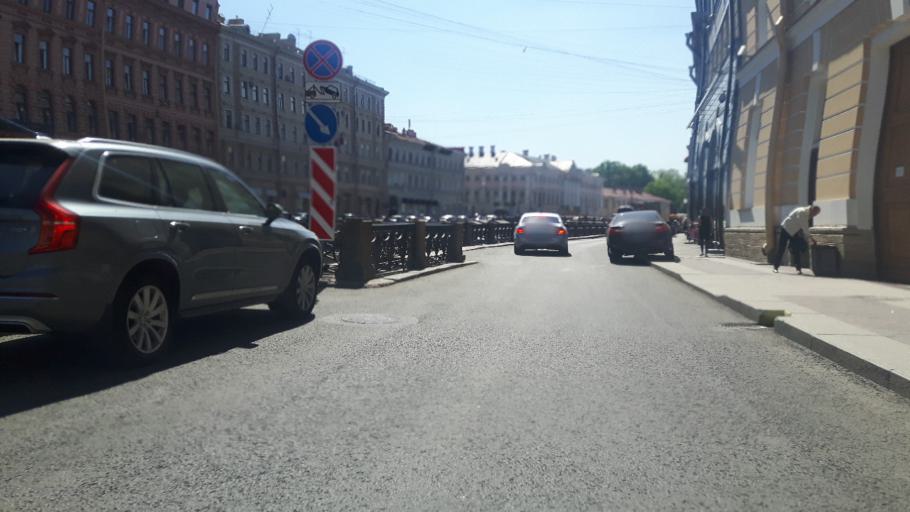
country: RU
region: St.-Petersburg
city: Saint Petersburg
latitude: 59.9376
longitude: 30.3195
